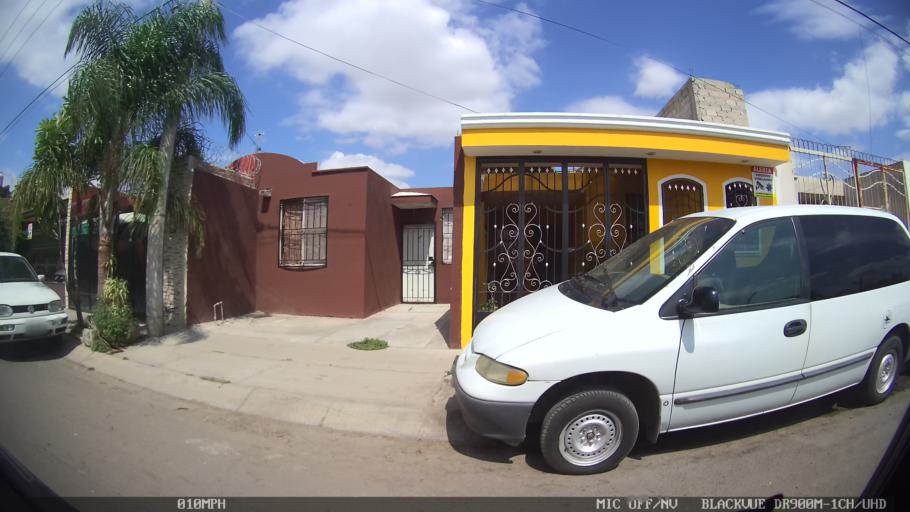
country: MX
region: Jalisco
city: Tonala
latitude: 20.6595
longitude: -103.2441
